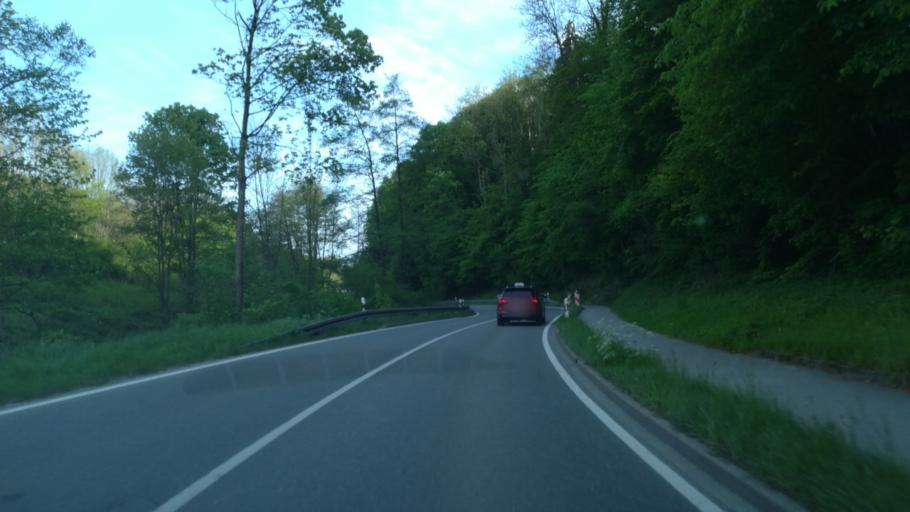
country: DE
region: Baden-Wuerttemberg
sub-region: Freiburg Region
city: Stockach
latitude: 47.8690
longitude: 9.0035
